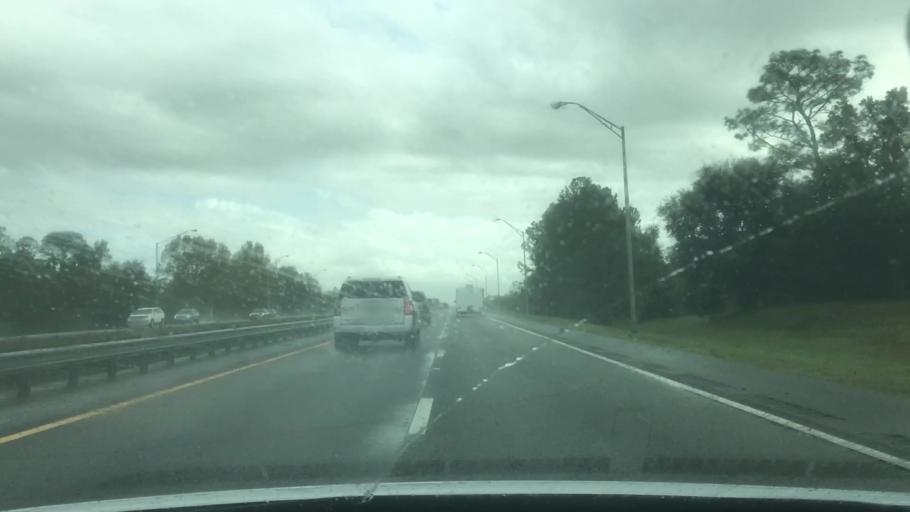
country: US
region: Florida
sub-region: Duval County
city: Jacksonville
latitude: 30.3335
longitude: -81.5351
